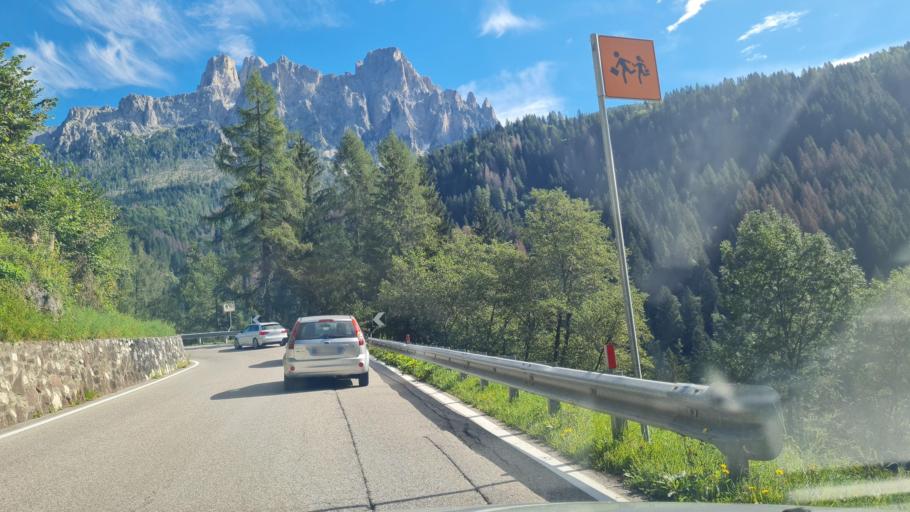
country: IT
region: Trentino-Alto Adige
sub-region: Provincia di Trento
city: Siror
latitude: 46.2050
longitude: 11.8189
